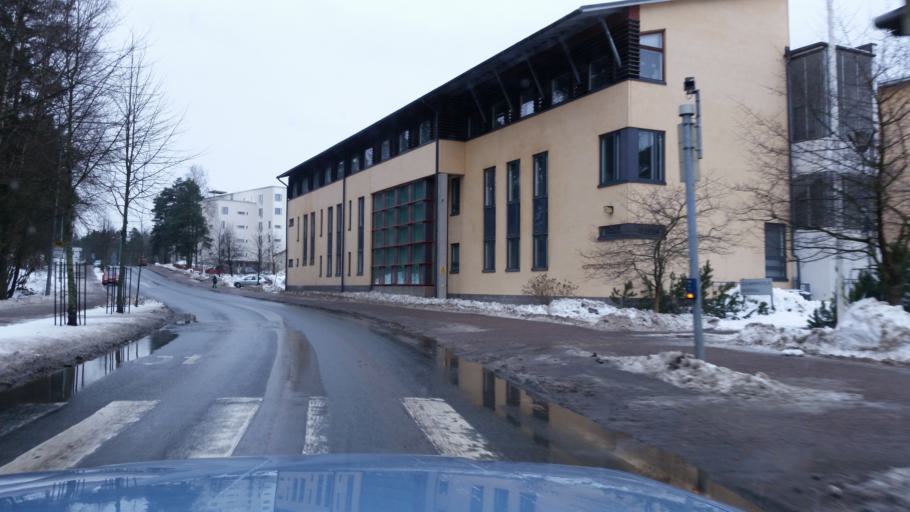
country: FI
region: Uusimaa
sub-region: Helsinki
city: Vantaa
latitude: 60.2454
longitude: 25.0780
